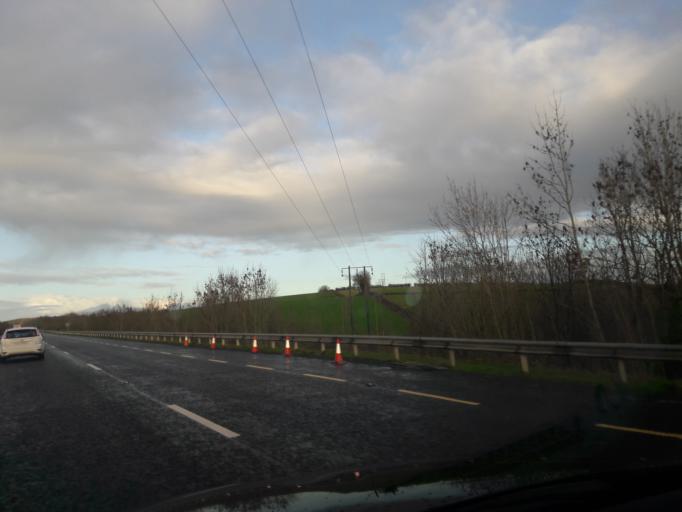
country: IE
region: Ulster
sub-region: County Monaghan
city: Carrickmacross
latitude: 54.0031
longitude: -6.7147
